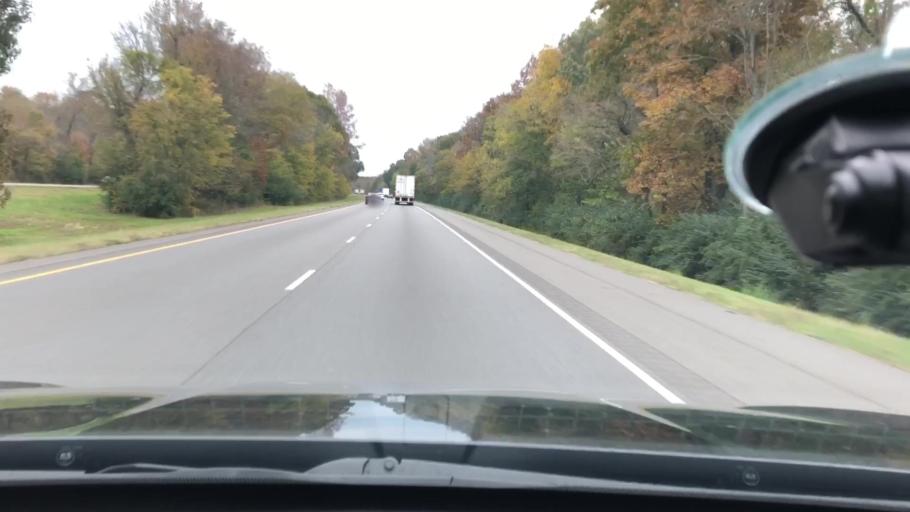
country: US
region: Arkansas
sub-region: Hempstead County
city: Hope
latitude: 33.6605
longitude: -93.6433
